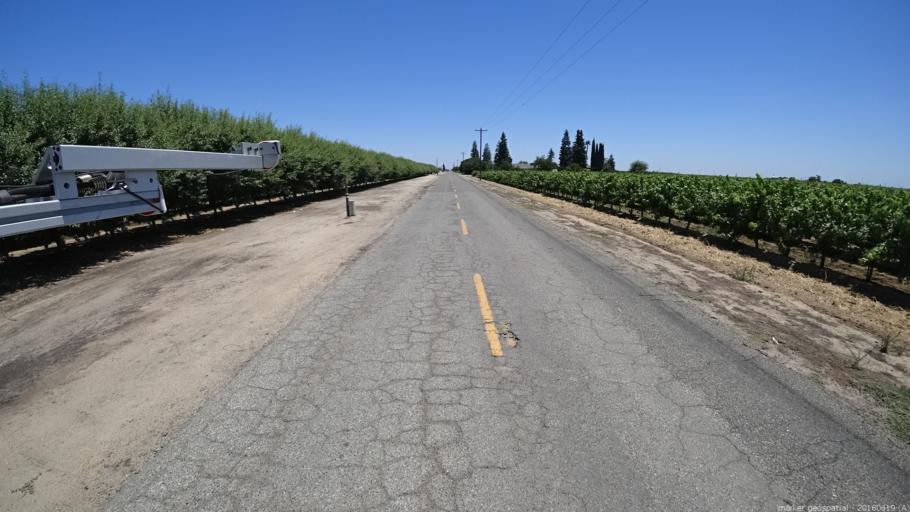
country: US
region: California
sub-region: Madera County
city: Parkwood
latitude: 36.8659
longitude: -120.0626
